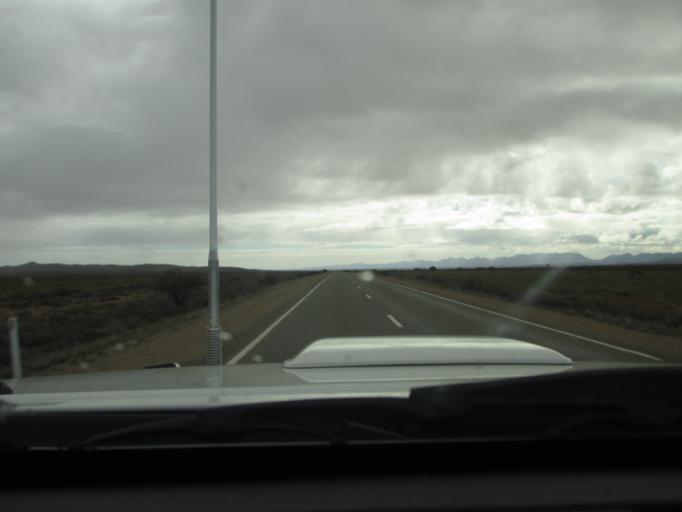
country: AU
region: South Australia
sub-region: Flinders Ranges
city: Quorn
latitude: -31.5314
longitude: 138.4259
